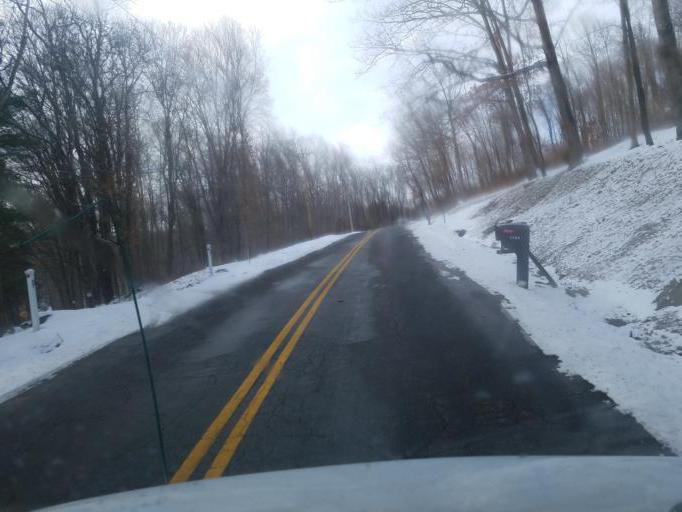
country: US
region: Ohio
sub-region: Holmes County
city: Millersburg
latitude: 40.4602
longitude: -81.9145
